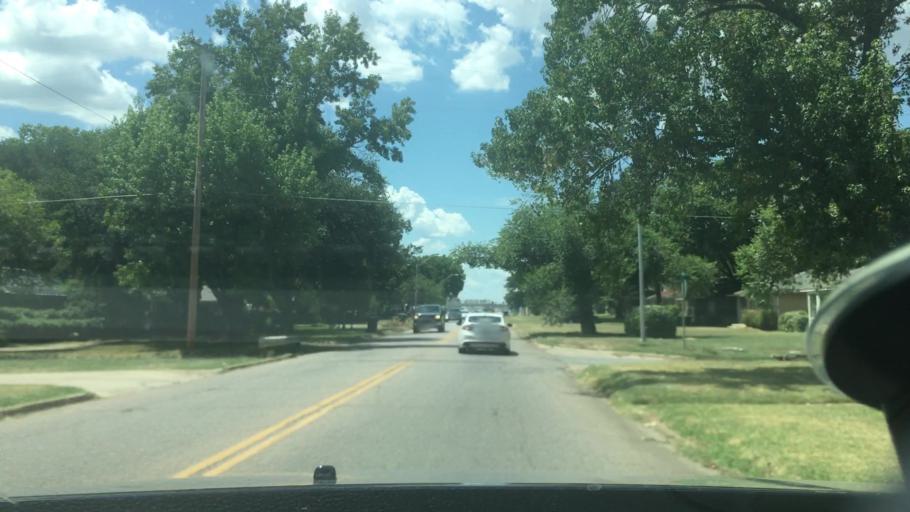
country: US
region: Oklahoma
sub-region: Bryan County
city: Durant
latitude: 33.9960
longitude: -96.3970
